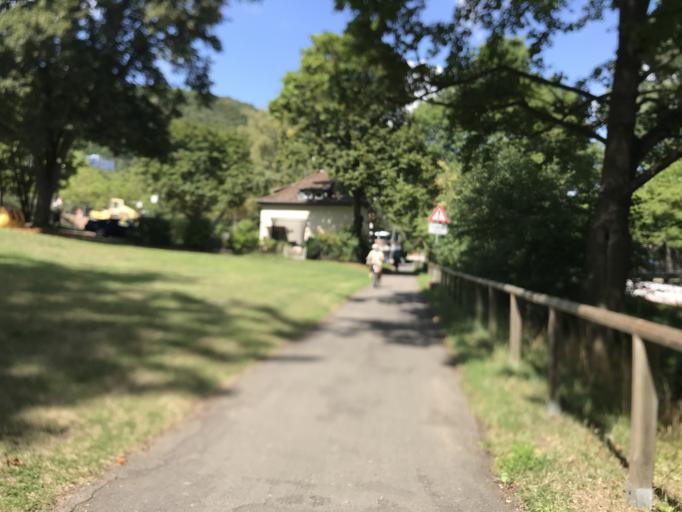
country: DE
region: Rheinland-Pfalz
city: Bad Munster am Stein-Ebernburg
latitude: 49.8240
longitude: 7.8509
